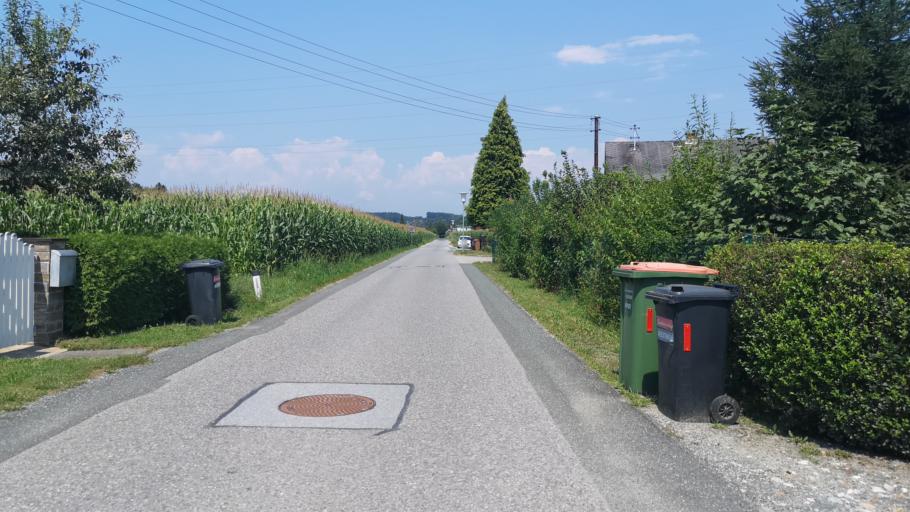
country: AT
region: Styria
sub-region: Politischer Bezirk Deutschlandsberg
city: Rassach
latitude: 46.8151
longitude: 15.2705
